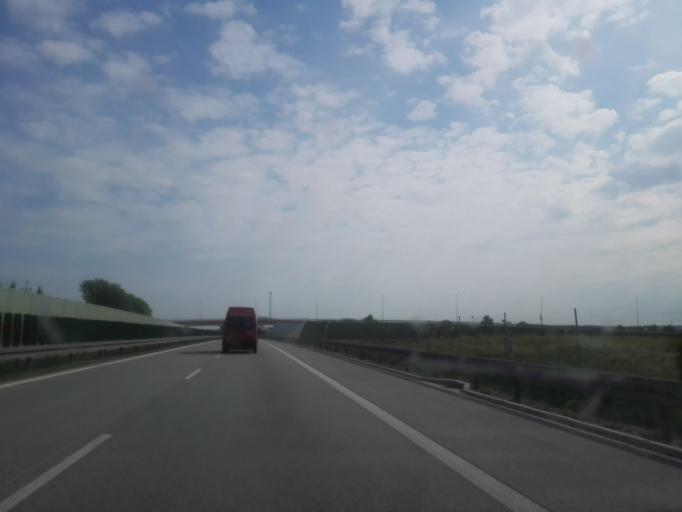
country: PL
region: Lodz Voivodeship
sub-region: Powiat rawski
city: Rawa Mazowiecka
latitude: 51.7545
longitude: 20.2549
